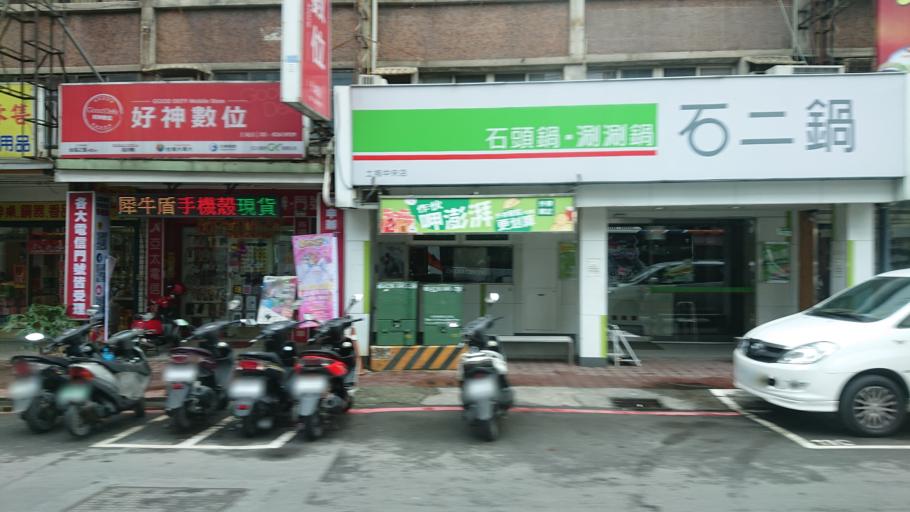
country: TW
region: Taipei
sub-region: Taipei
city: Banqiao
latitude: 24.9731
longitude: 121.4405
